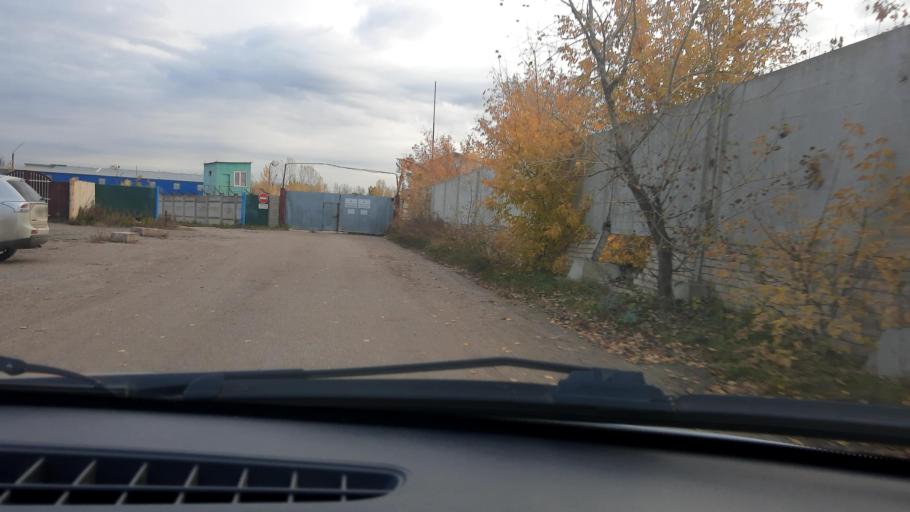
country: RU
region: Bashkortostan
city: Ufa
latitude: 54.7479
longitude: 55.9127
